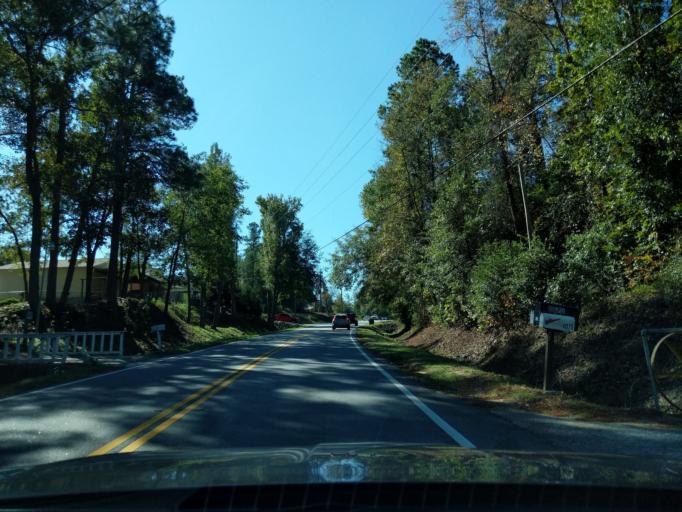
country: US
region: Georgia
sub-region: Richmond County
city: Hephzibah
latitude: 33.3341
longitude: -82.0078
